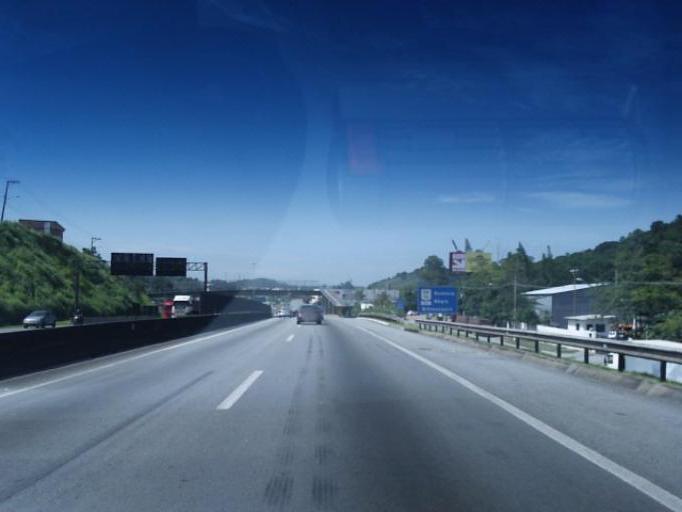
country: BR
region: Sao Paulo
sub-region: Embu
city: Embu
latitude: -23.6679
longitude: -46.8556
